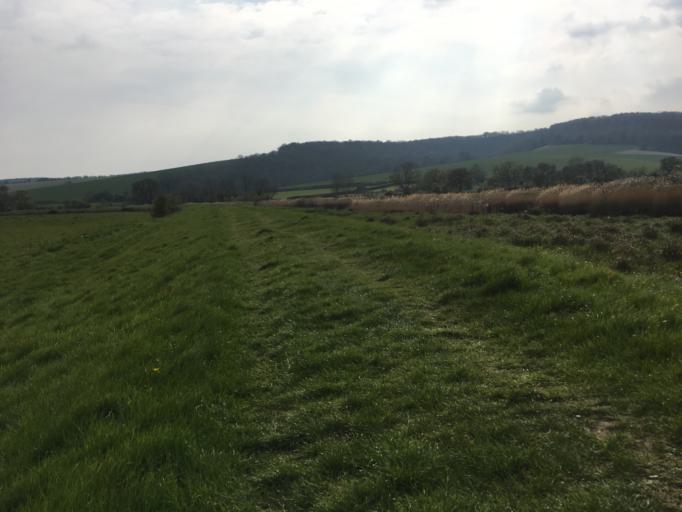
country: GB
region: England
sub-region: West Sussex
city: Arundel
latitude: 50.9066
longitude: -0.5541
